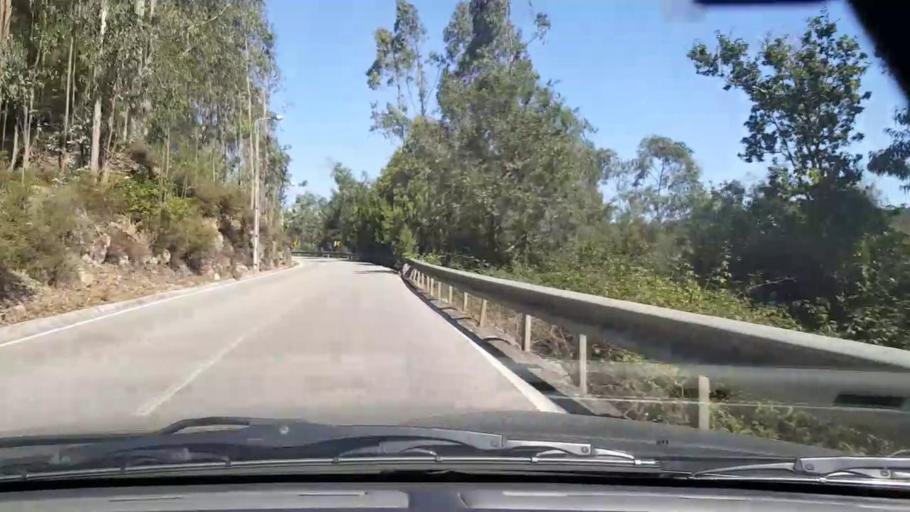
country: PT
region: Braga
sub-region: Vila Nova de Famalicao
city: Ribeirao
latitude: 41.3388
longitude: -8.6234
